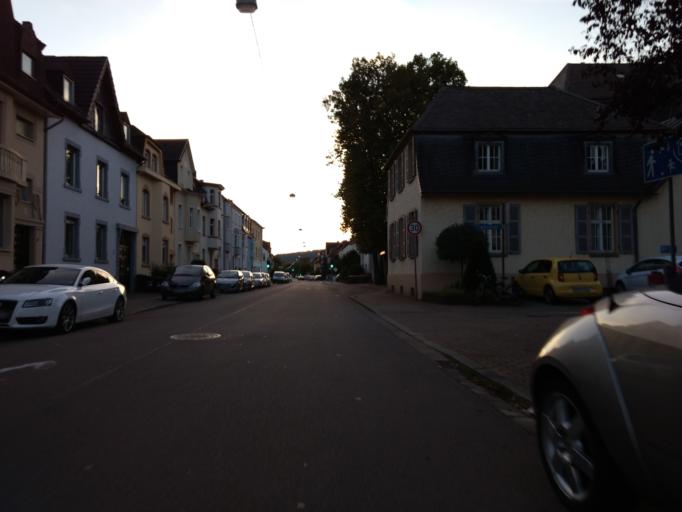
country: DE
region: Saarland
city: Dillingen
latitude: 49.3586
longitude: 6.7288
